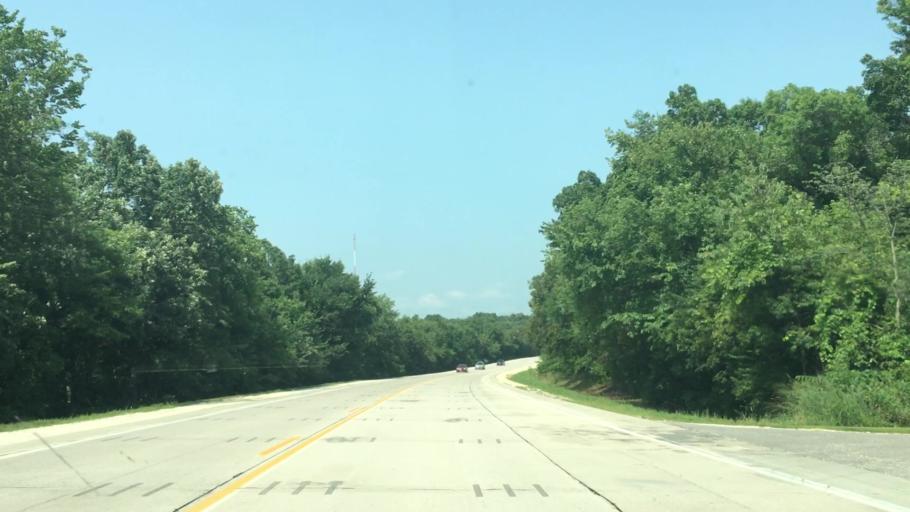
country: US
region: Iowa
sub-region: Winneshiek County
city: Decorah
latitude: 43.3386
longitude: -91.8119
